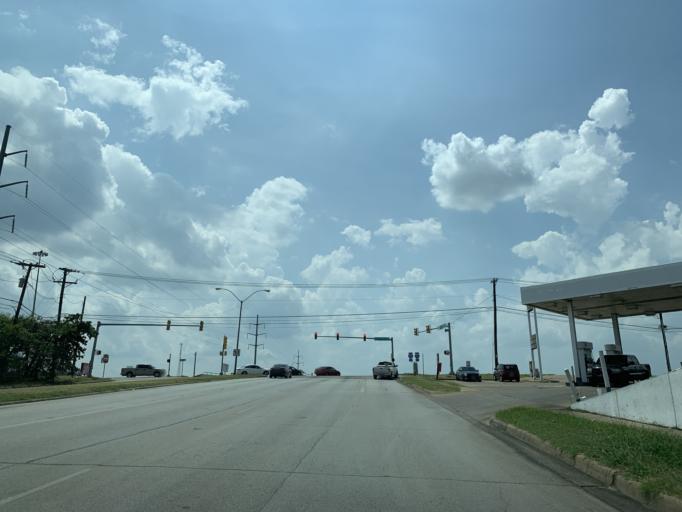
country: US
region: Texas
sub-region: Tarrant County
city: Richland Hills
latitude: 32.7664
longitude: -97.2114
